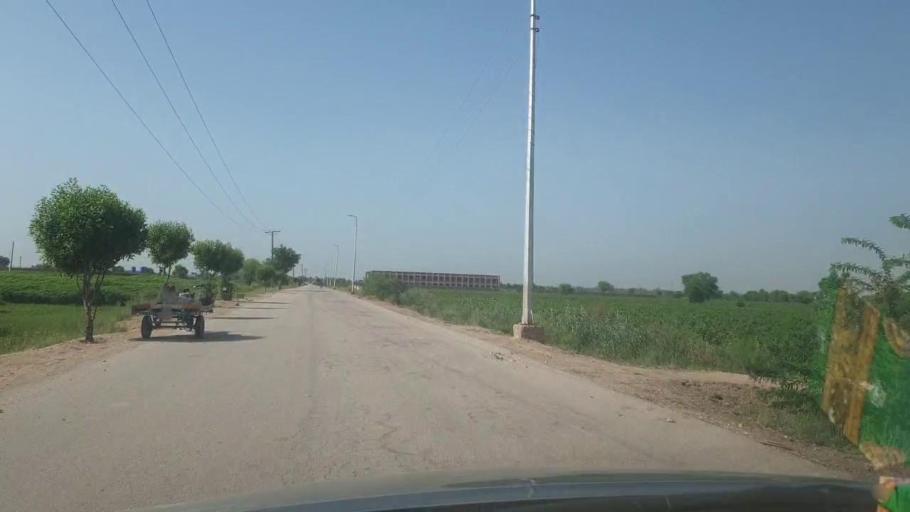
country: PK
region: Sindh
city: Rohri
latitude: 27.5187
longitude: 69.0361
